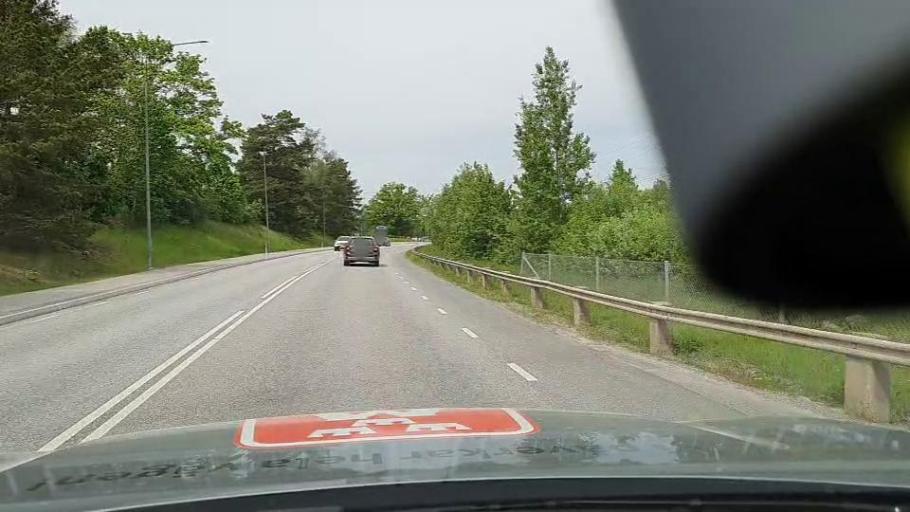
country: SE
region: Soedermanland
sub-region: Flens Kommun
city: Flen
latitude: 59.0650
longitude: 16.5923
